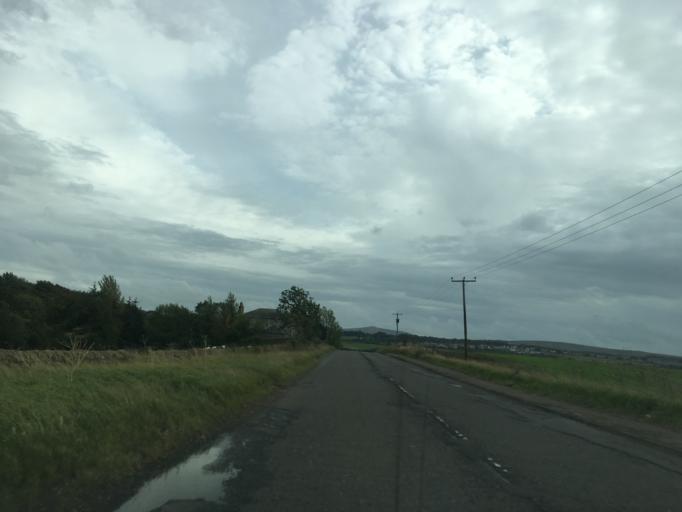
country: GB
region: Scotland
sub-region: West Lothian
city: Kirknewton
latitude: 55.9081
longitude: -3.4070
